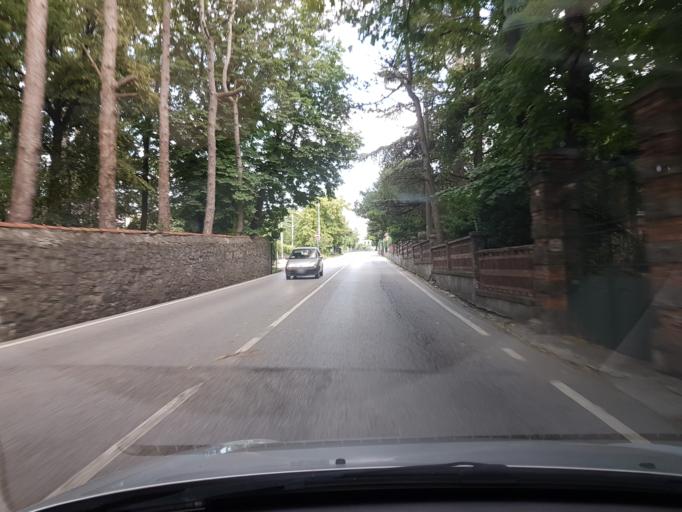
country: IT
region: Friuli Venezia Giulia
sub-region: Provincia di Trieste
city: Villa Opicina
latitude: 45.6873
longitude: 13.7930
